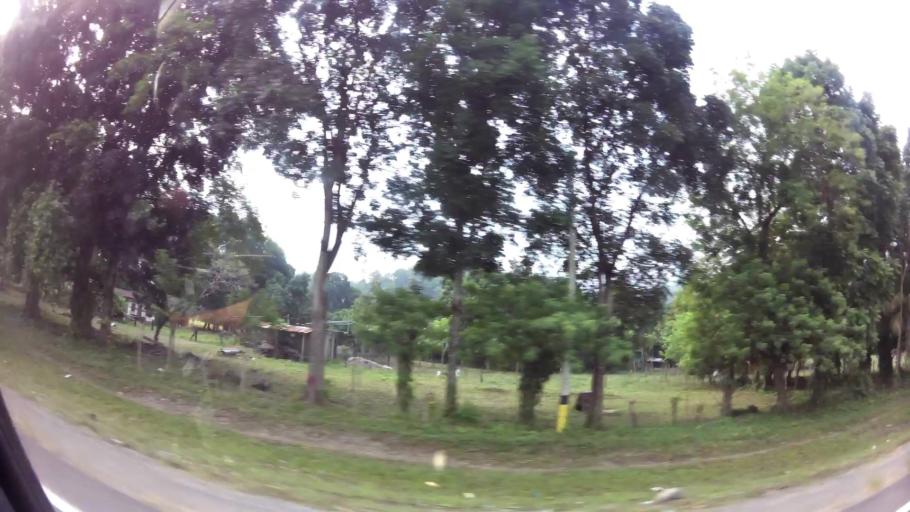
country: HN
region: Yoro
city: Toyos
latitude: 15.5129
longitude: -87.6725
